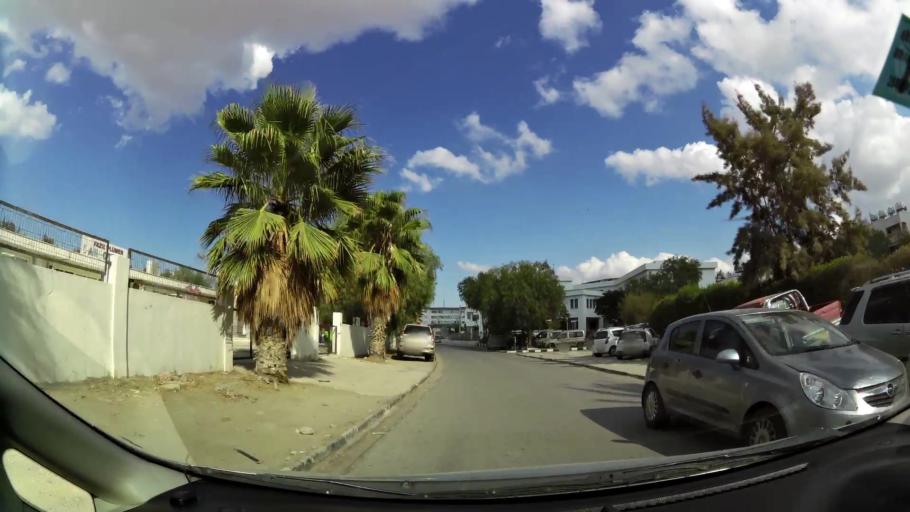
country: CY
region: Lefkosia
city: Nicosia
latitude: 35.1942
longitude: 33.3495
